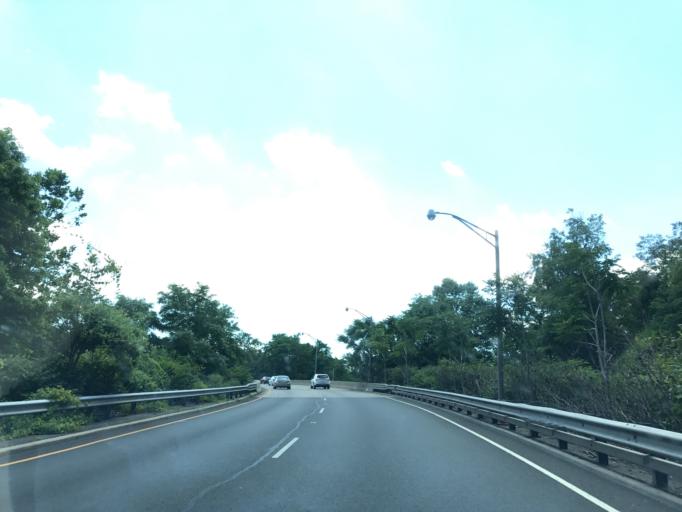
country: US
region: New Jersey
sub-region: Morris County
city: Morris Plains
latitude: 40.8115
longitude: -74.4484
